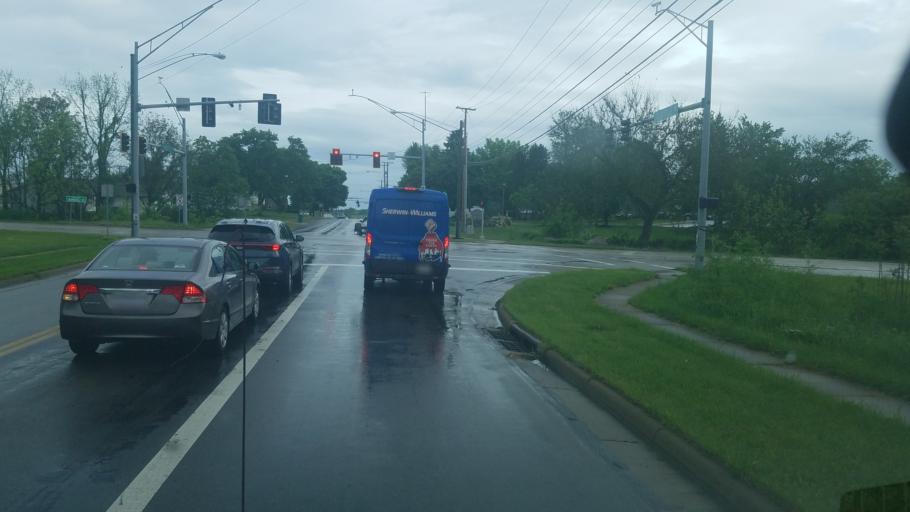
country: US
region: Ohio
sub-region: Wayne County
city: Wooster
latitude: 40.8414
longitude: -81.9396
